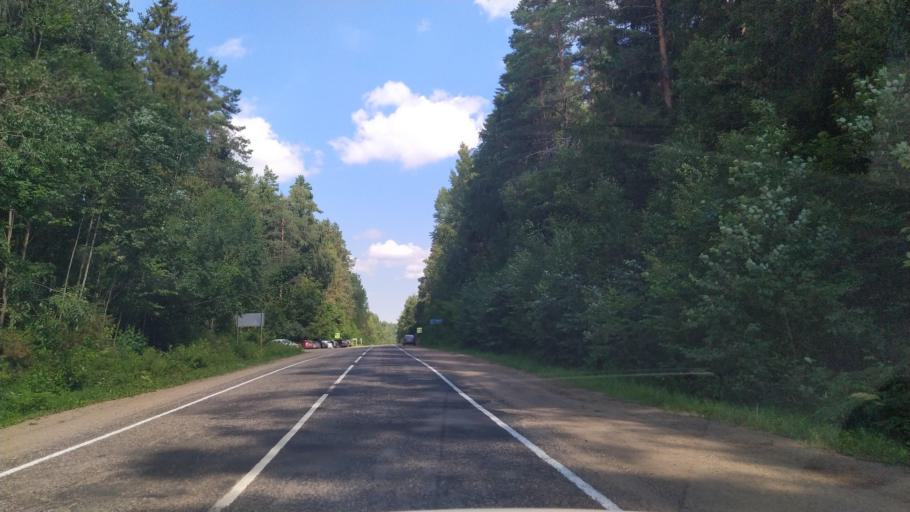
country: RU
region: Pskov
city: Pushkinskiye Gory
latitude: 57.0563
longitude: 28.9454
